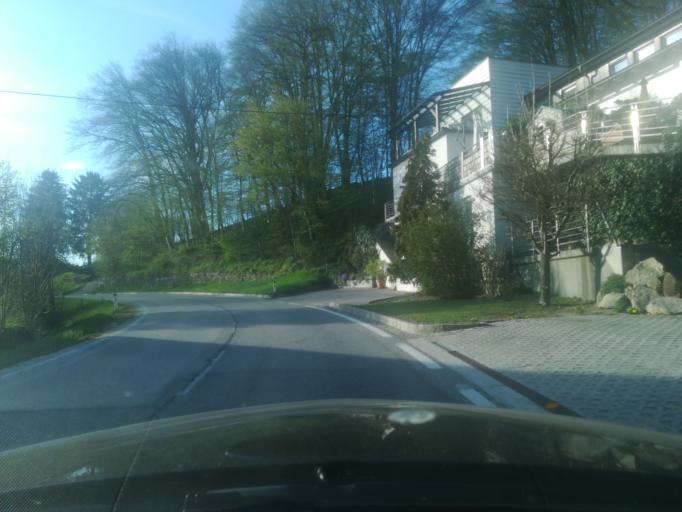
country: AT
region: Upper Austria
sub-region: Politischer Bezirk Perg
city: Bad Kreuzen
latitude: 48.2332
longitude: 14.8426
